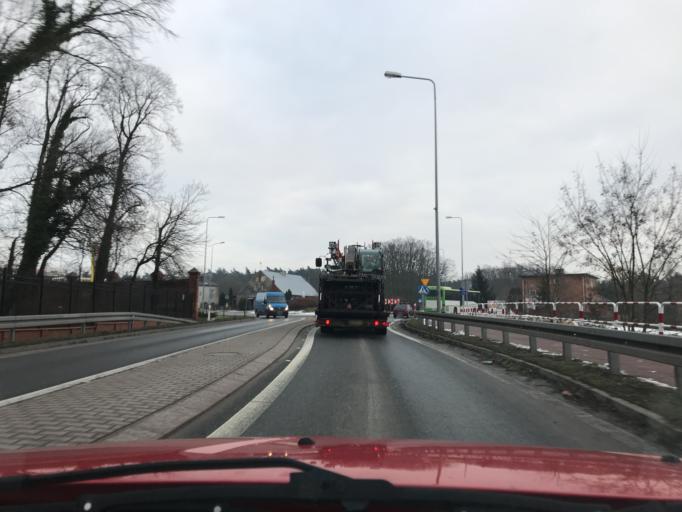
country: PL
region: Greater Poland Voivodeship
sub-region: Powiat pleszewski
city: Goluchow
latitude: 51.8486
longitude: 17.9368
